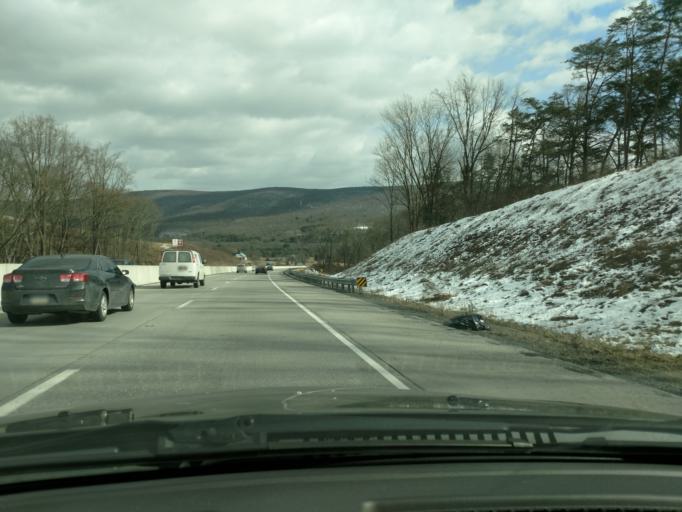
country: US
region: Pennsylvania
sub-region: Schuylkill County
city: Orwigsburg
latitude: 40.6145
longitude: -76.0392
